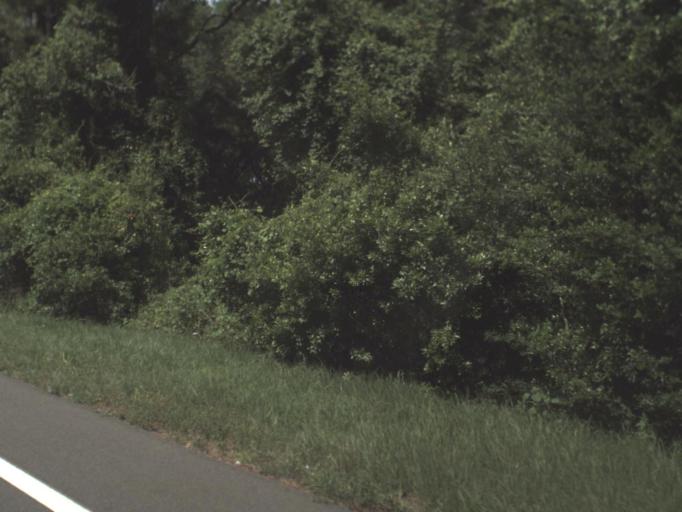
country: US
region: Florida
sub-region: Duval County
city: Atlantic Beach
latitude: 30.4856
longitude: -81.4399
